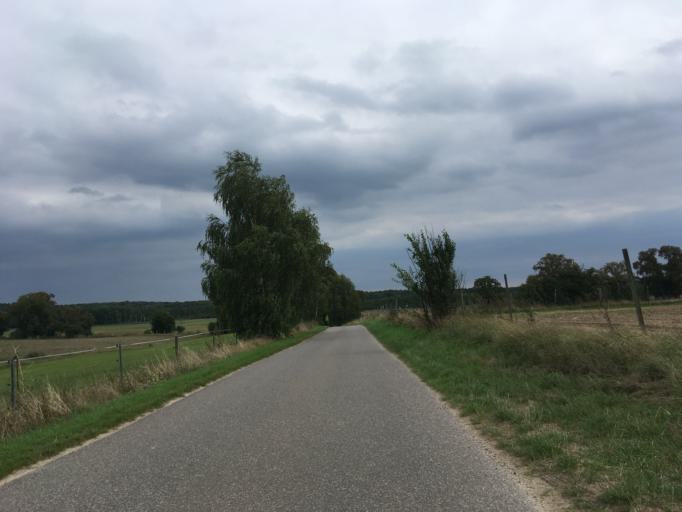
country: DE
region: Brandenburg
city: Joachimsthal
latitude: 53.0230
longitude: 13.7737
